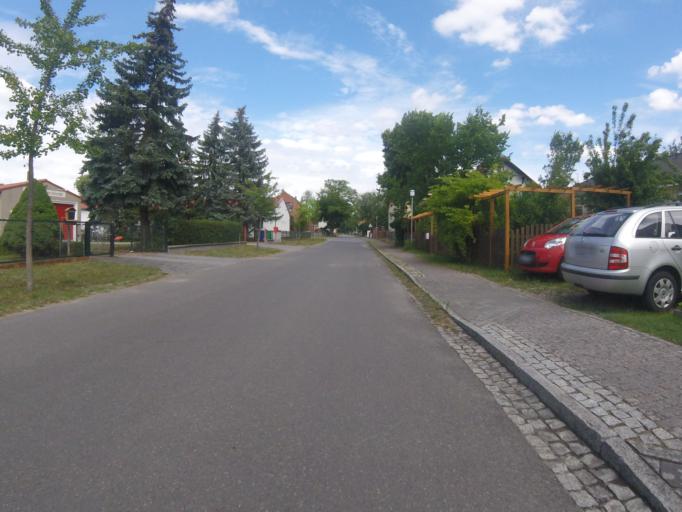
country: DE
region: Brandenburg
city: Bestensee
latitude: 52.2380
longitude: 13.7078
